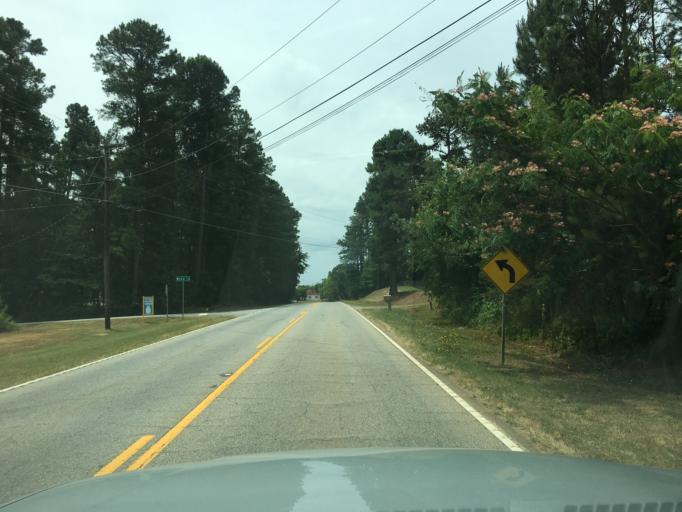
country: US
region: South Carolina
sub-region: Anderson County
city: Centerville
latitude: 34.5348
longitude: -82.8032
